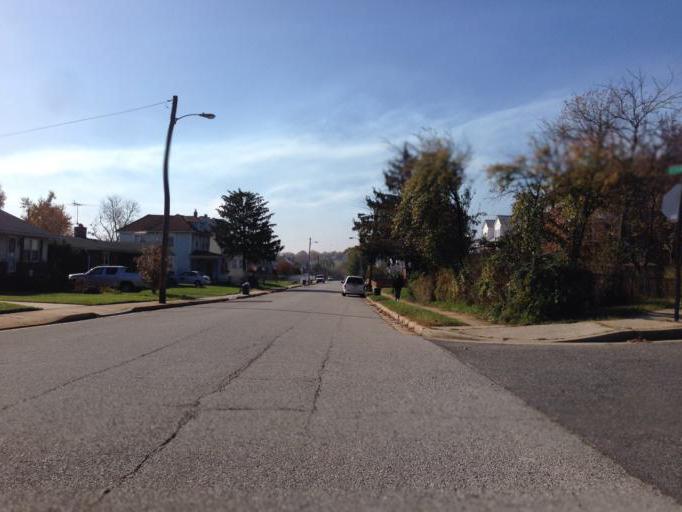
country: US
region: Maryland
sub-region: Baltimore County
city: Dundalk
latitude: 39.2840
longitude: -76.5317
